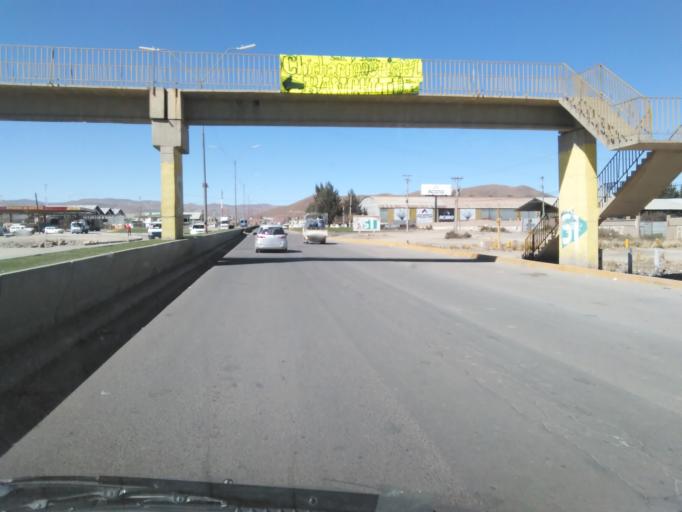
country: BO
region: Oruro
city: Oruro
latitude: -17.9772
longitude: -67.0624
